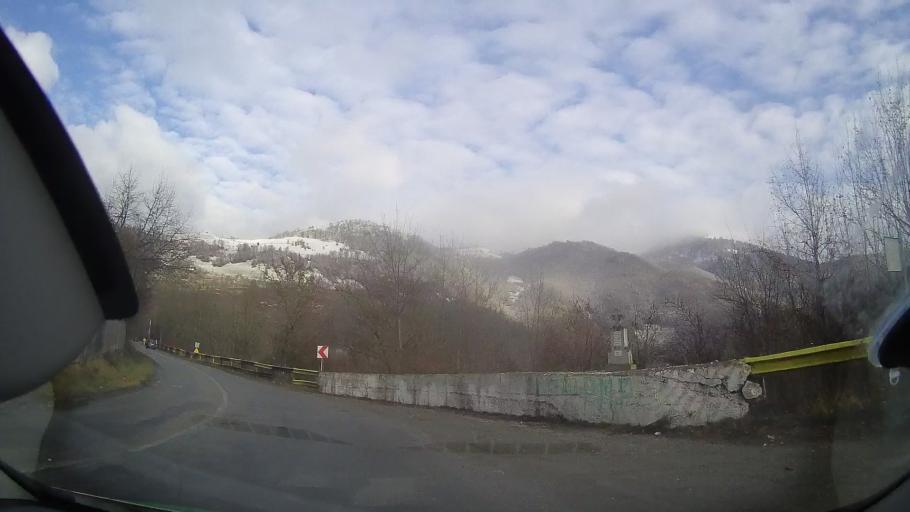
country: RO
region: Alba
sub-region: Comuna Lupsa
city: Lupsa
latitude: 46.3805
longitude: 23.2308
